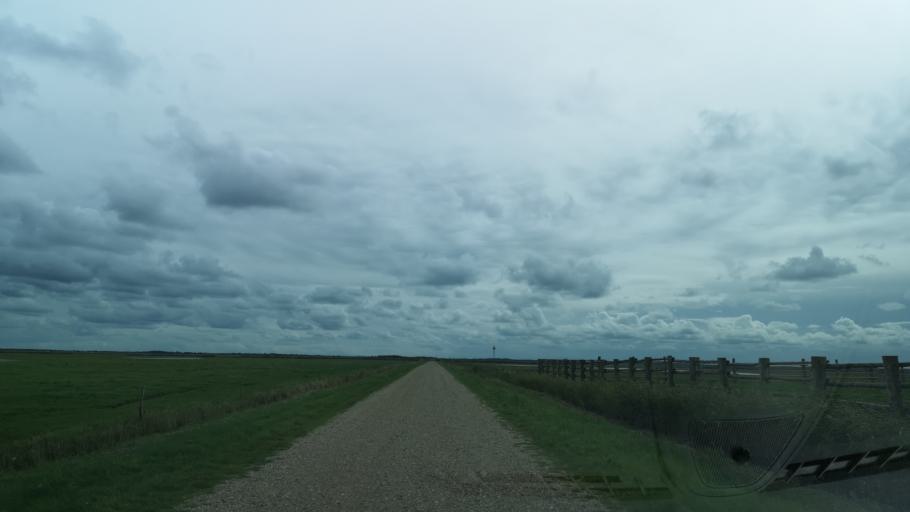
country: DK
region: Central Jutland
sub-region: Ringkobing-Skjern Kommune
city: Hvide Sande
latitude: 55.8774
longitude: 8.2250
